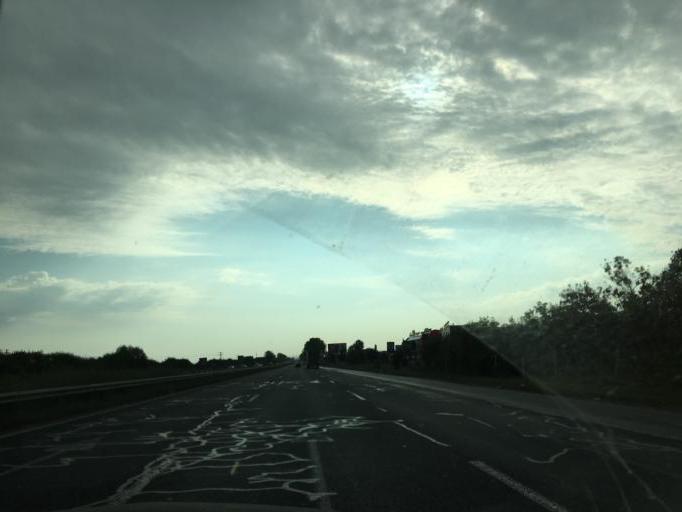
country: BG
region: Sofiya
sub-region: Obshtina Elin Pelin
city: Elin Pelin
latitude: 42.6316
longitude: 23.4601
